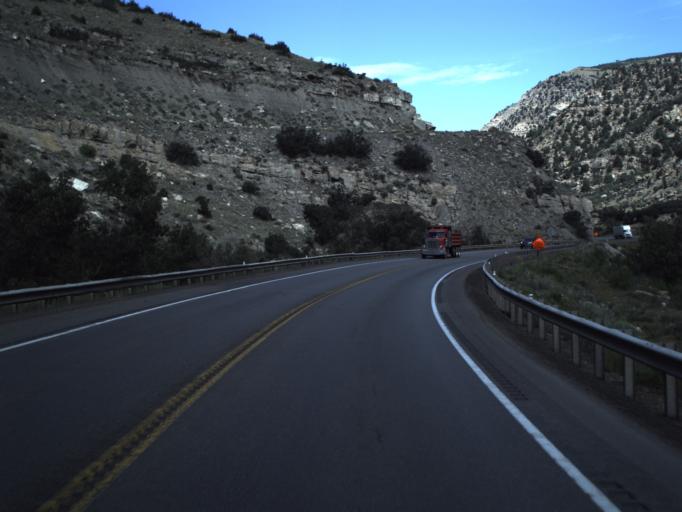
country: US
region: Utah
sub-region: Carbon County
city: Helper
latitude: 39.7728
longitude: -110.9110
